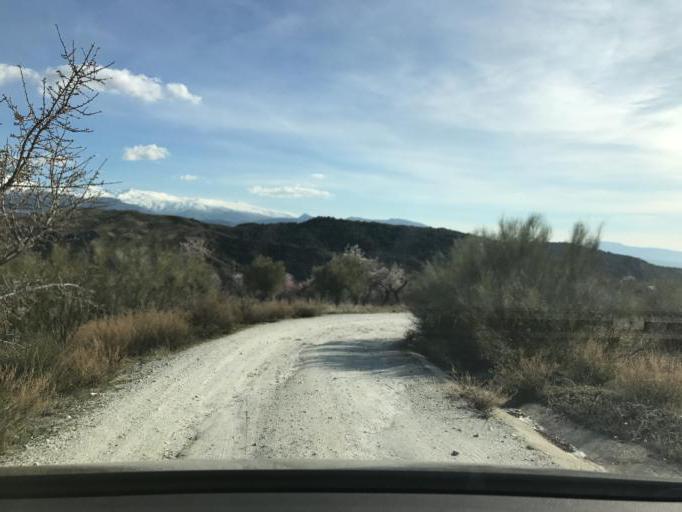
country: ES
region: Andalusia
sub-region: Provincia de Granada
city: Huetor Santillan
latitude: 37.2192
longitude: -3.5046
